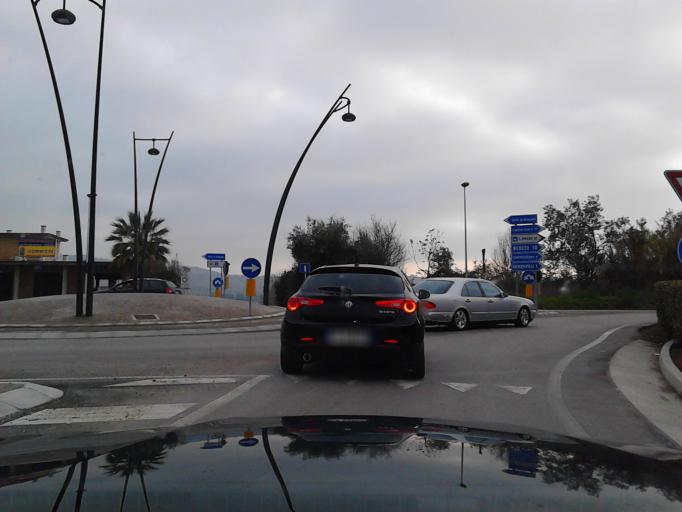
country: IT
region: Abruzzo
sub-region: Provincia di Teramo
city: Villa Rosa
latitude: 42.8335
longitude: 13.8931
